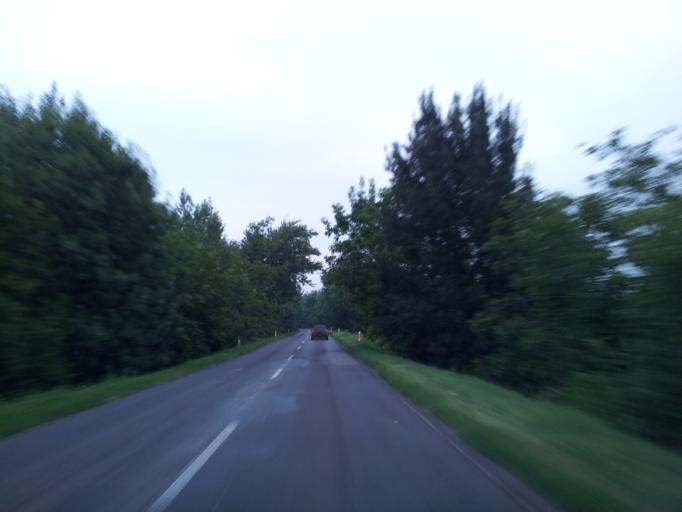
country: HU
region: Tolna
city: Tolna
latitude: 46.4282
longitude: 18.7970
